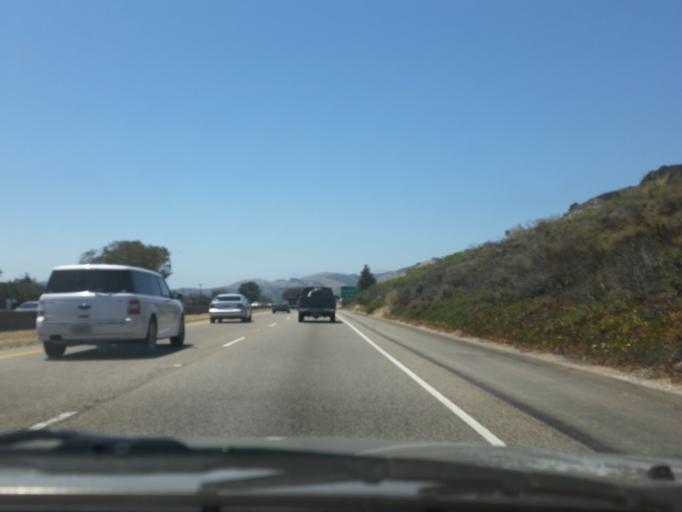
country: US
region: California
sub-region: San Luis Obispo County
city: Pismo Beach
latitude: 35.1617
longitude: -120.6815
